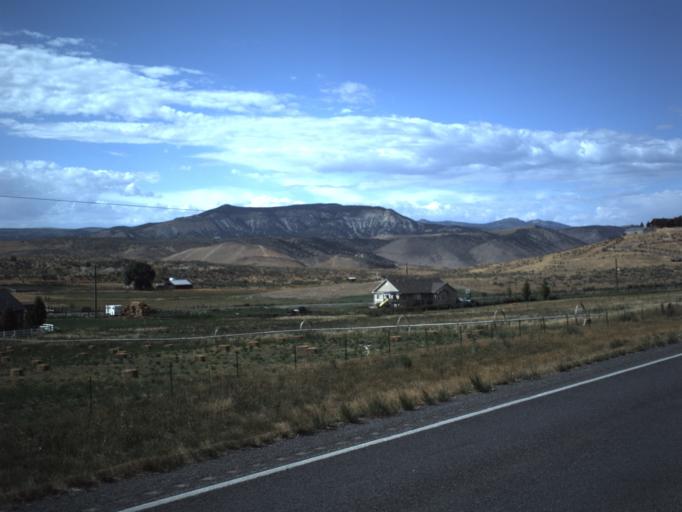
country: US
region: Utah
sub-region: Sanpete County
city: Manti
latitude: 39.2068
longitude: -111.6905
